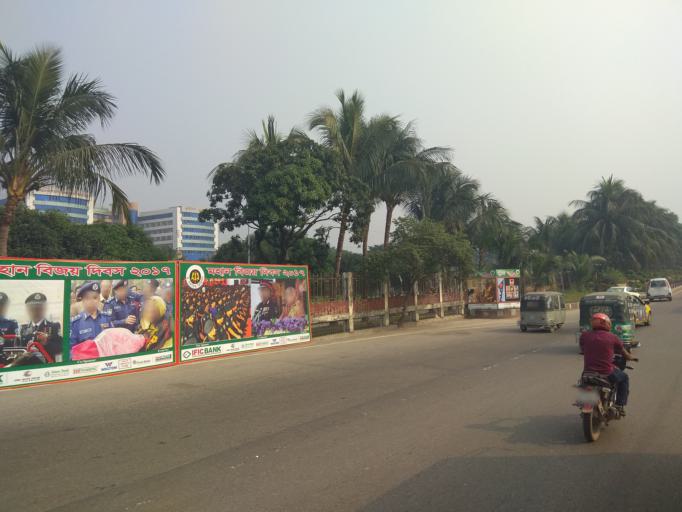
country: BD
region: Dhaka
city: Tungi
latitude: 23.8171
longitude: 90.4079
